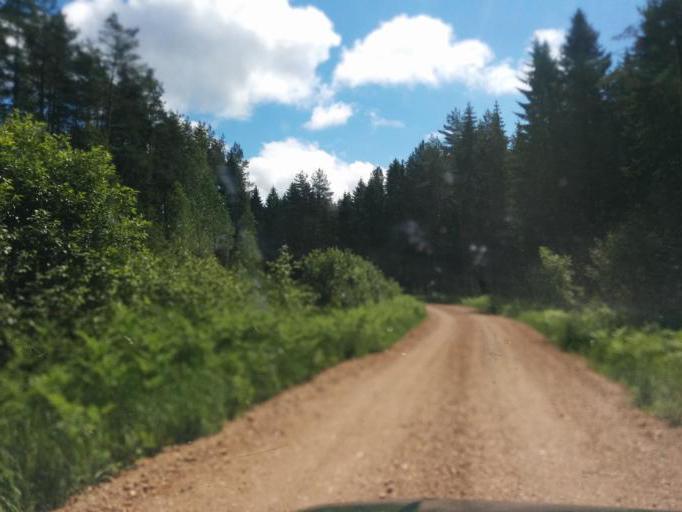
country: LV
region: Vilaka
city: Vilaka
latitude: 57.3355
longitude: 27.7029
